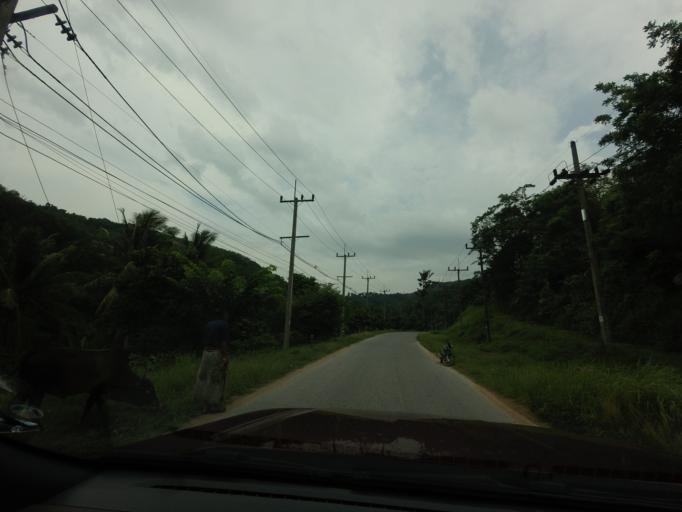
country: TH
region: Yala
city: Than To
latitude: 6.1686
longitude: 101.2682
